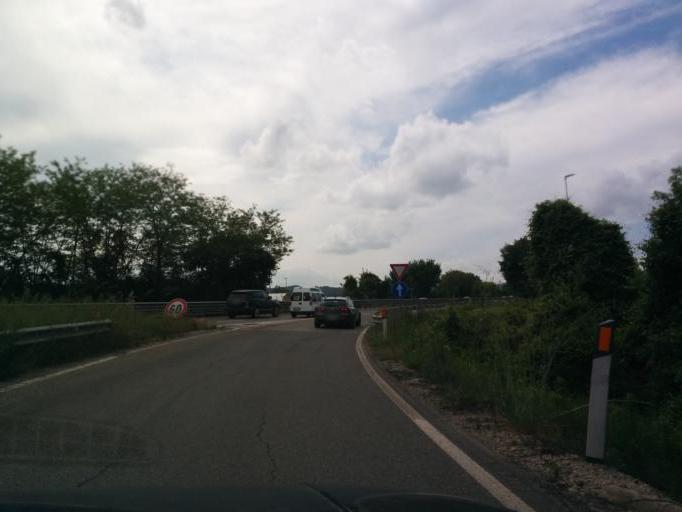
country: IT
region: Tuscany
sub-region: Province of Florence
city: Sambuca
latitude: 43.5911
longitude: 11.1993
